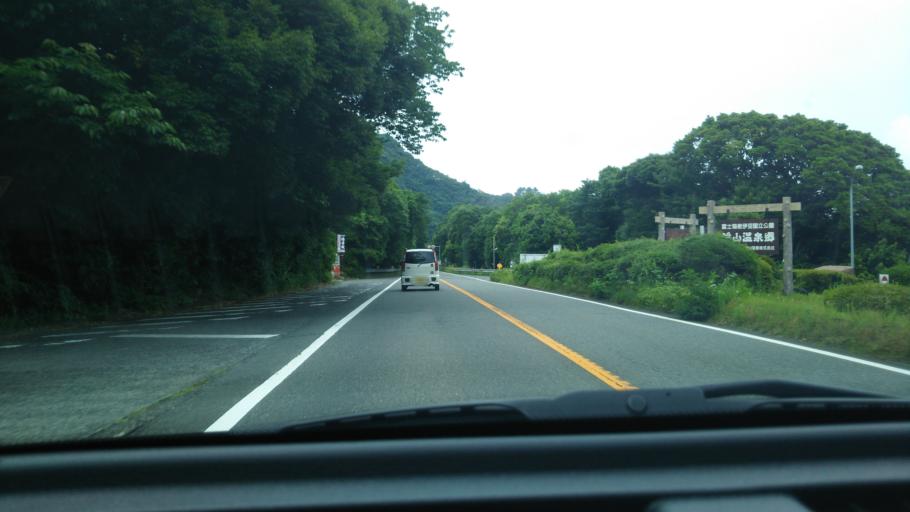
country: JP
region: Shizuoka
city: Ito
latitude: 34.8677
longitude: 139.0957
